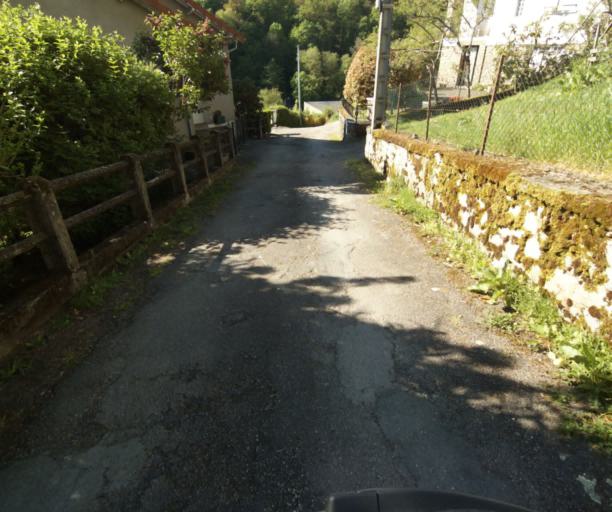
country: FR
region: Limousin
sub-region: Departement de la Correze
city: Tulle
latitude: 45.2764
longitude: 1.7791
